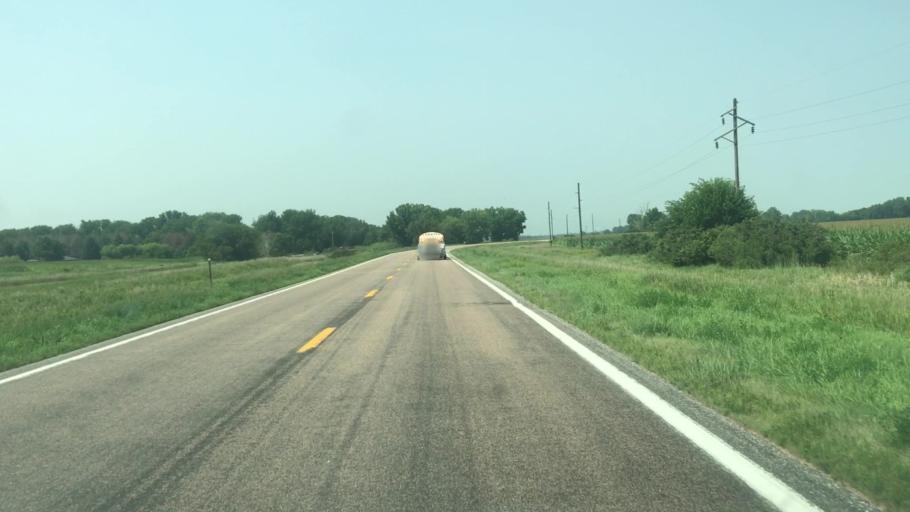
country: US
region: Nebraska
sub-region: Sherman County
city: Loup City
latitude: 41.2325
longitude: -98.9362
